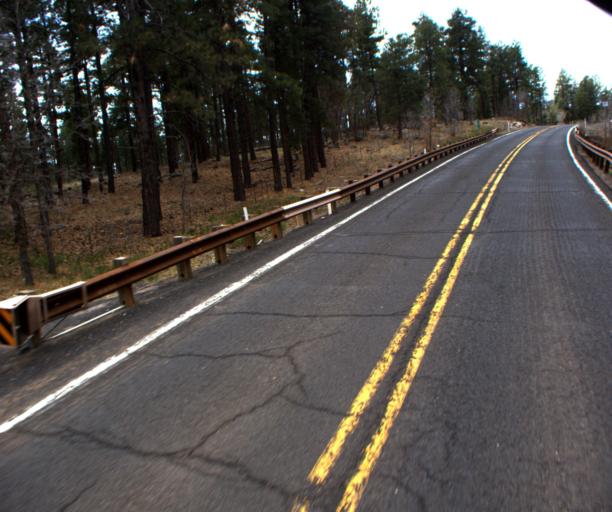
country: US
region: Arizona
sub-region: Coconino County
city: Kachina Village
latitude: 35.1101
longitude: -111.7168
